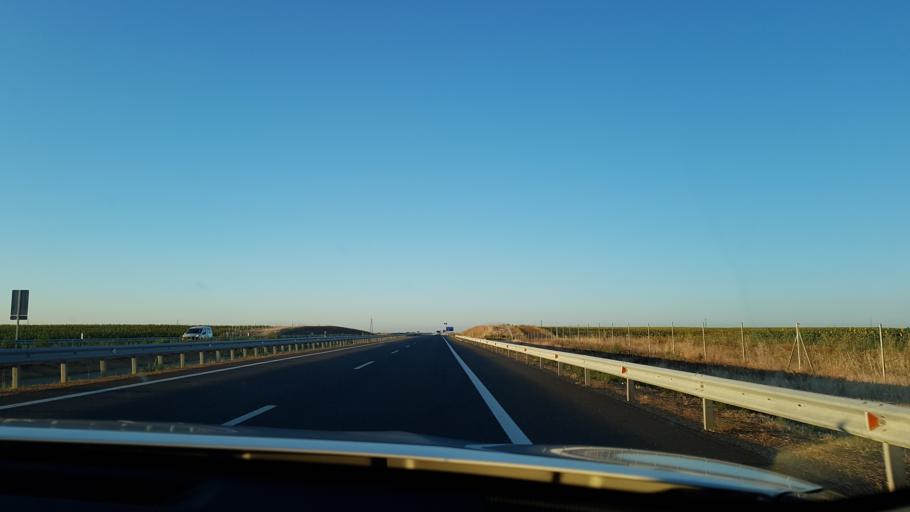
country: ES
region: Castille and Leon
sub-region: Provincia de Zamora
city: Roales
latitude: 41.5943
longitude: -5.7809
